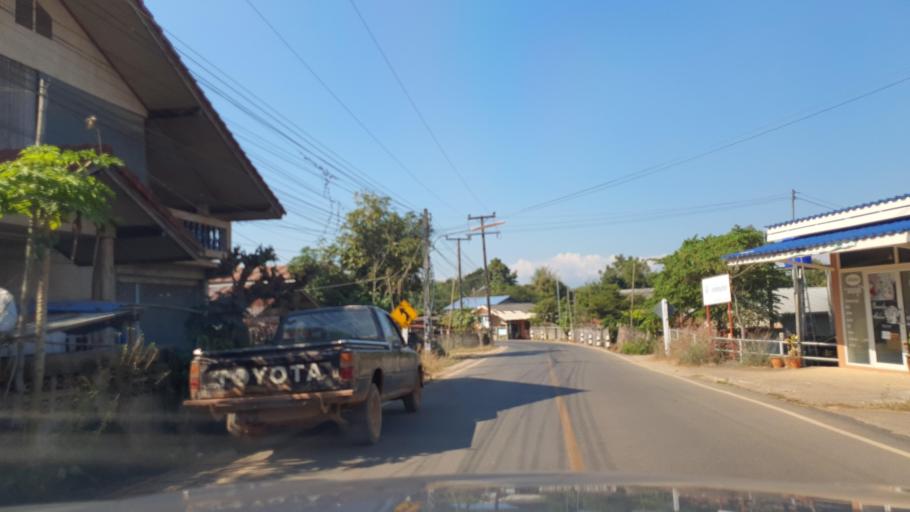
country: TH
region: Nan
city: Pua
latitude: 19.1337
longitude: 100.9316
